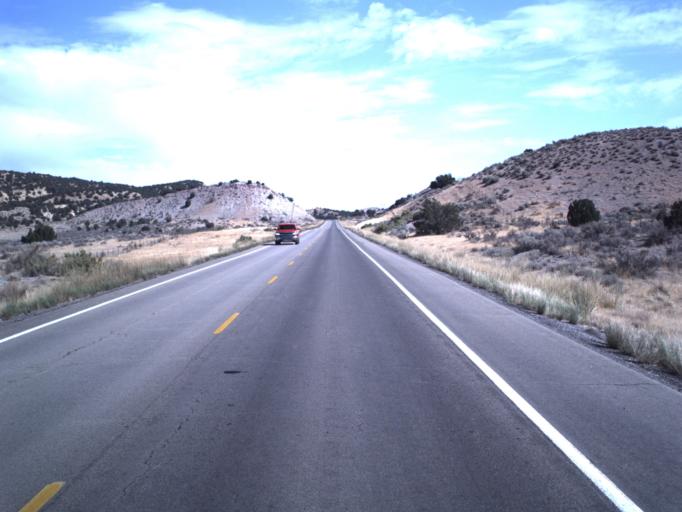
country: US
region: Utah
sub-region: Sanpete County
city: Gunnison
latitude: 39.3701
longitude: -111.9290
